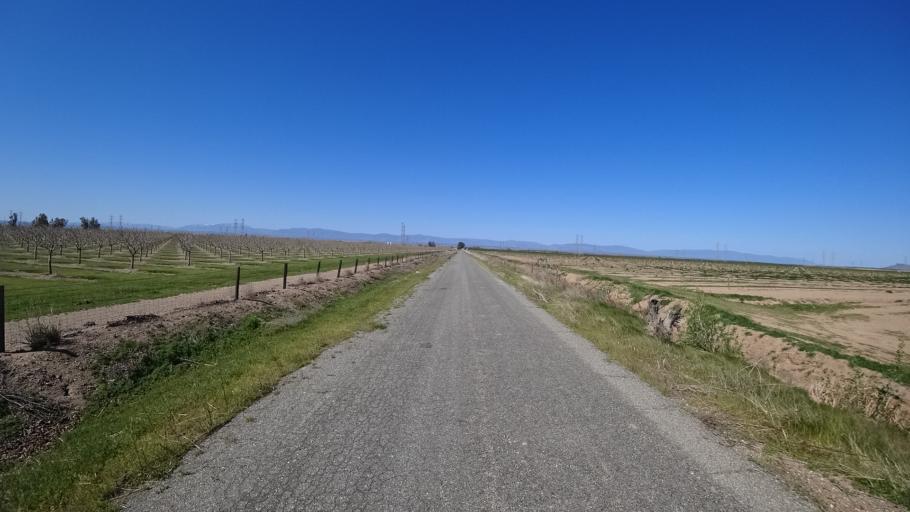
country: US
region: California
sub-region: Glenn County
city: Orland
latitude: 39.6538
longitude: -122.2589
